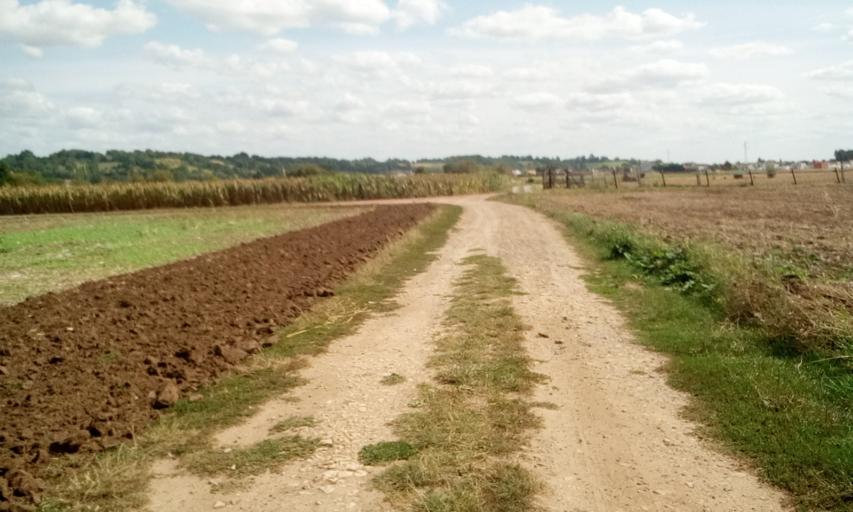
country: FR
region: Lower Normandy
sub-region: Departement du Calvados
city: Argences
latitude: 49.1328
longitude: -0.1837
